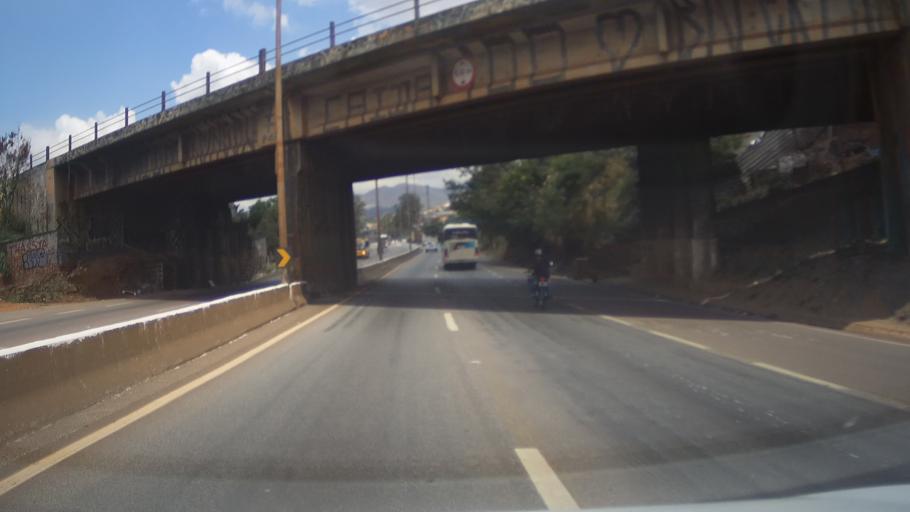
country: BR
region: Minas Gerais
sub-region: Contagem
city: Contagem
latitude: -19.9560
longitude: -44.0031
